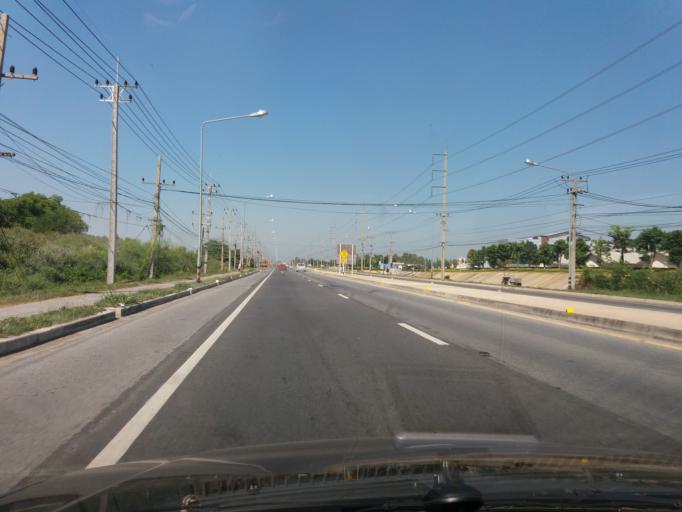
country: TH
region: Chai Nat
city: Manorom
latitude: 15.2768
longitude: 100.0951
